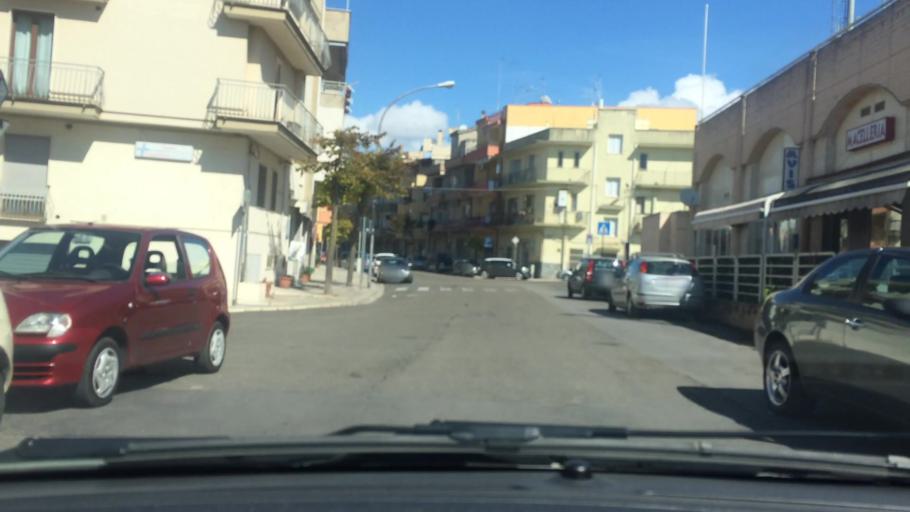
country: IT
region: Basilicate
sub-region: Provincia di Matera
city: Montescaglioso
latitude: 40.5465
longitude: 16.6671
